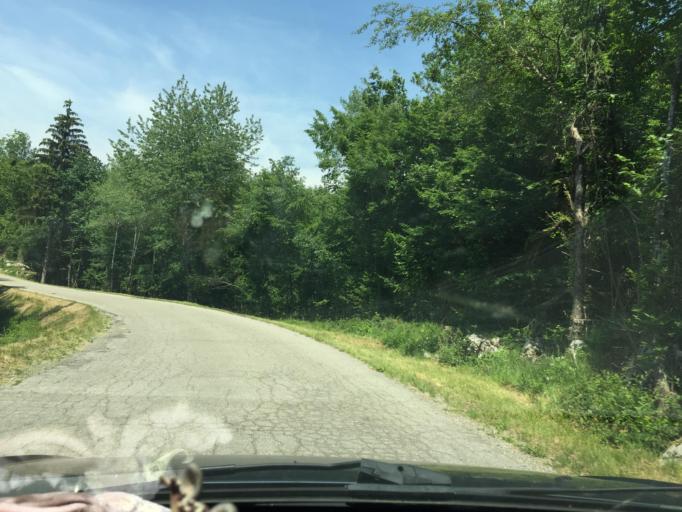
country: HR
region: Istarska
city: Buzet
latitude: 45.4609
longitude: 14.1355
